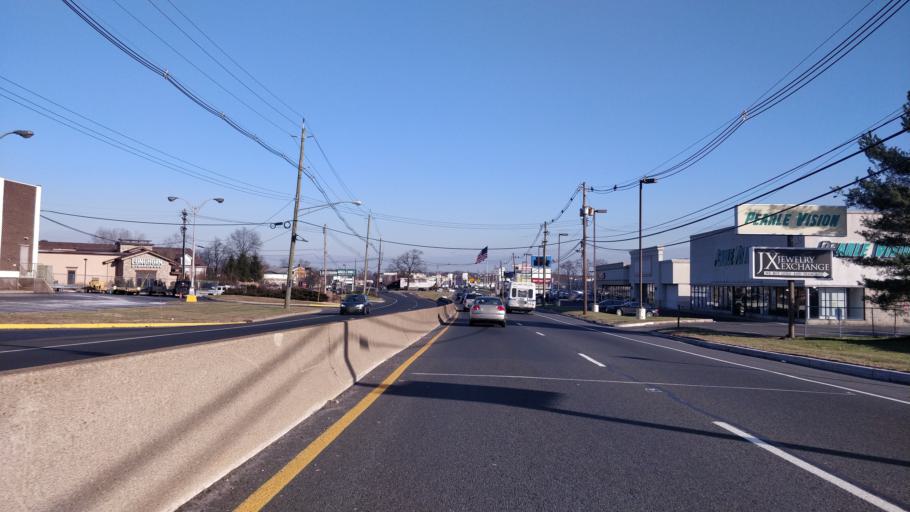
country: US
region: New Jersey
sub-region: Union County
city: Springfield
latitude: 40.6851
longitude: -74.3253
